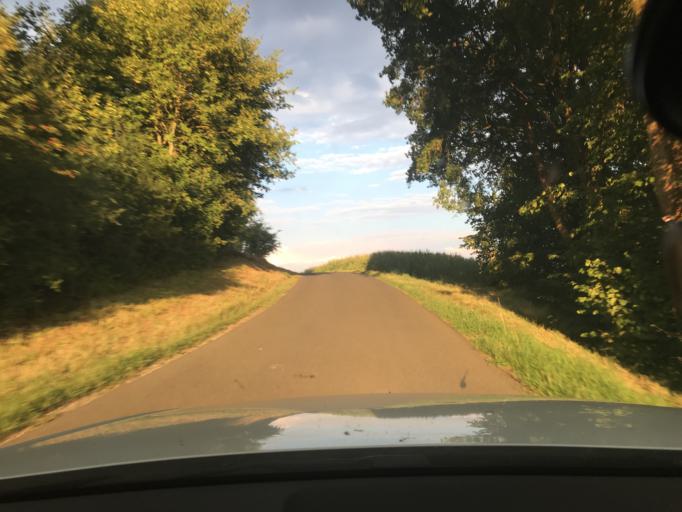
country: DE
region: Bavaria
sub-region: Upper Franconia
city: Pegnitz
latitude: 49.7468
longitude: 11.5800
